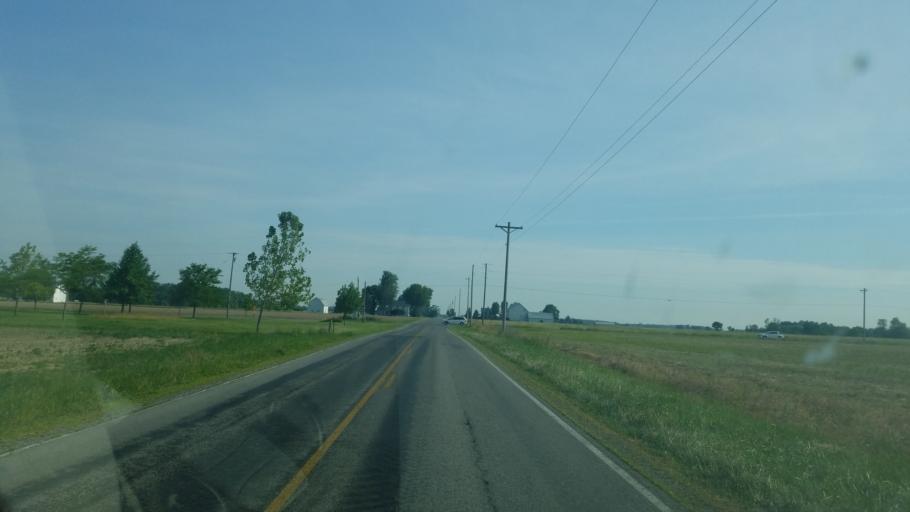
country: US
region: Ohio
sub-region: Hancock County
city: Arlington
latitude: 40.9495
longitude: -83.6987
